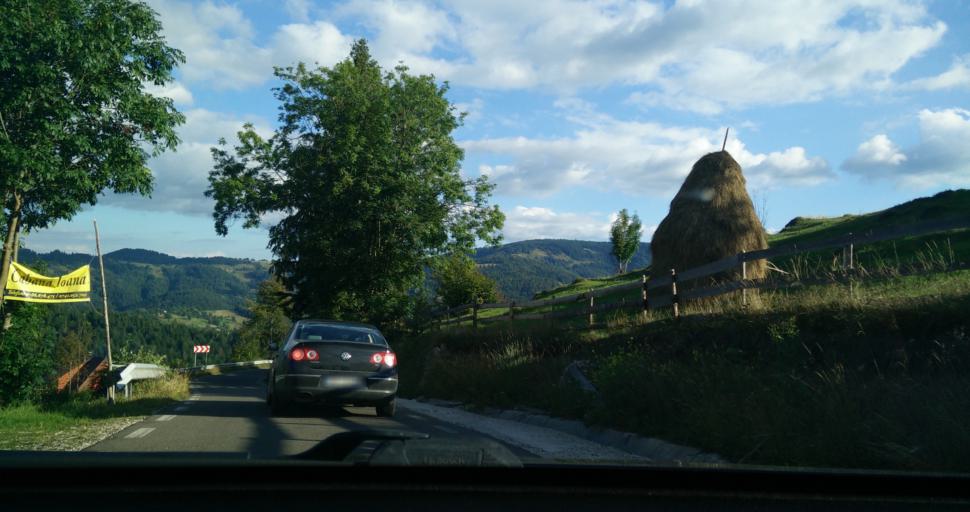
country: RO
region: Alba
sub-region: Comuna Scarisoara
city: Scarisoara
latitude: 46.4699
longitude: 22.8320
